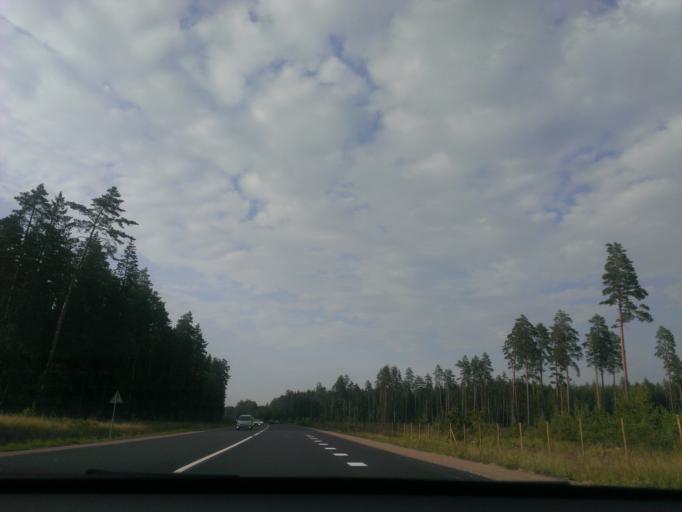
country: LV
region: Kekava
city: Kekava
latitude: 56.7221
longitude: 24.2530
